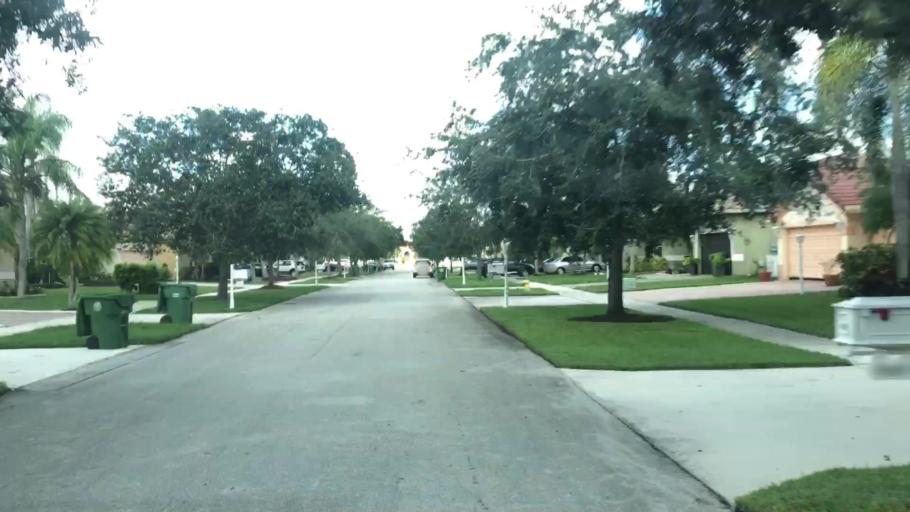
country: US
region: Florida
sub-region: Broward County
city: Southwest Ranches
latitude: 26.0326
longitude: -80.3662
